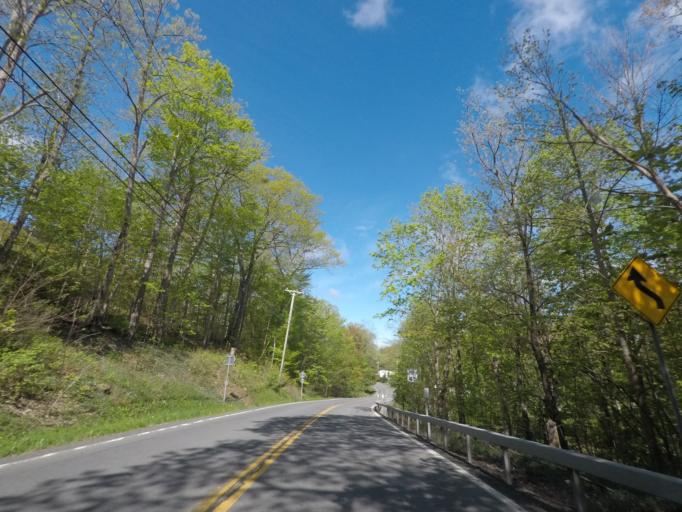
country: US
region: New York
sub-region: Albany County
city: Ravena
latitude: 42.4676
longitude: -73.8834
